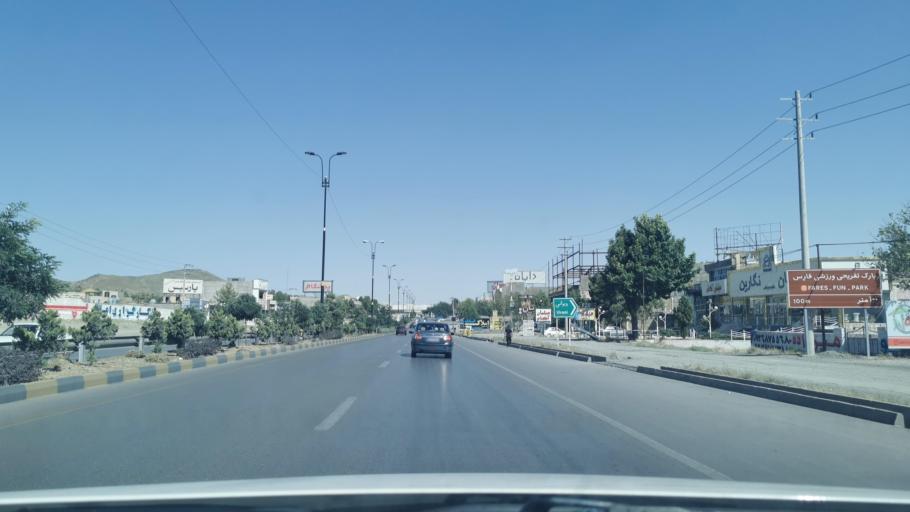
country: IR
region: Razavi Khorasan
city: Torqabeh
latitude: 36.3946
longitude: 59.3989
